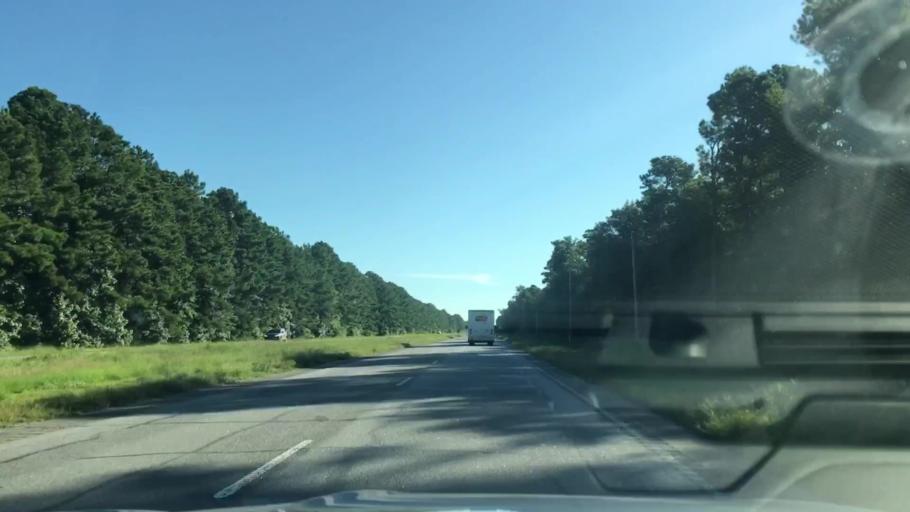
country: US
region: South Carolina
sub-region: Charleston County
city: Awendaw
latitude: 33.0624
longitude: -79.5357
